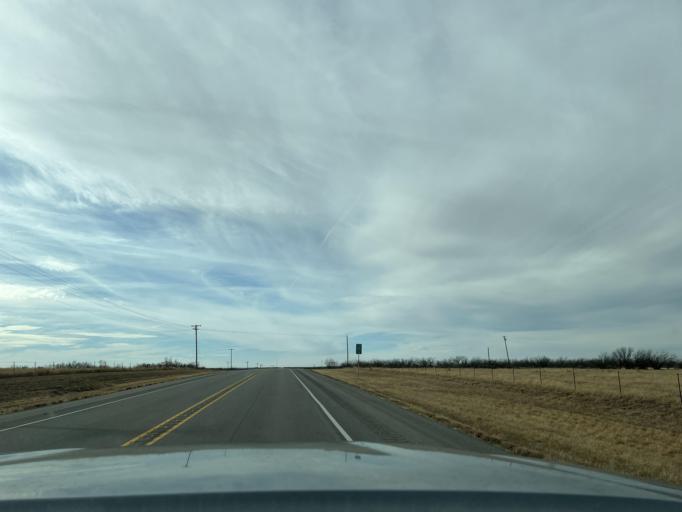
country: US
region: Texas
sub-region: Jones County
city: Anson
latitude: 32.7506
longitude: -99.6875
